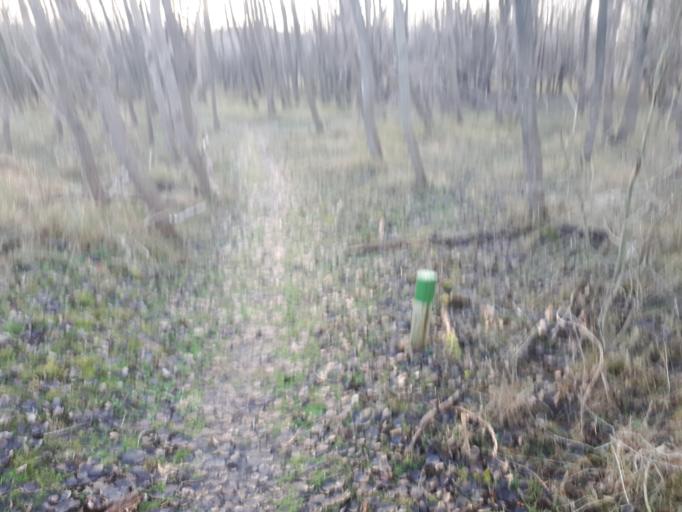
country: NL
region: South Holland
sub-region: Gemeente Wassenaar
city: Wassenaar
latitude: 52.1414
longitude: 4.3632
